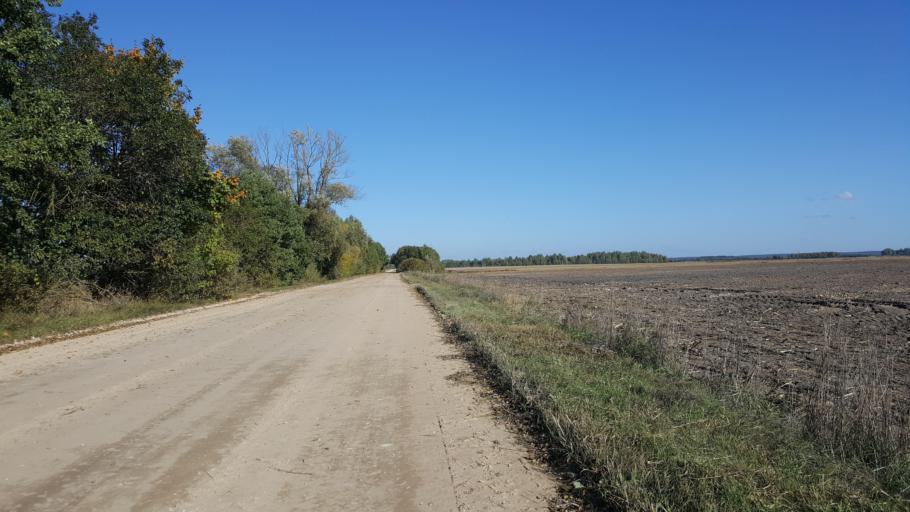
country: BY
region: Brest
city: Kamyanyets
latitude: 52.4255
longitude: 23.8799
